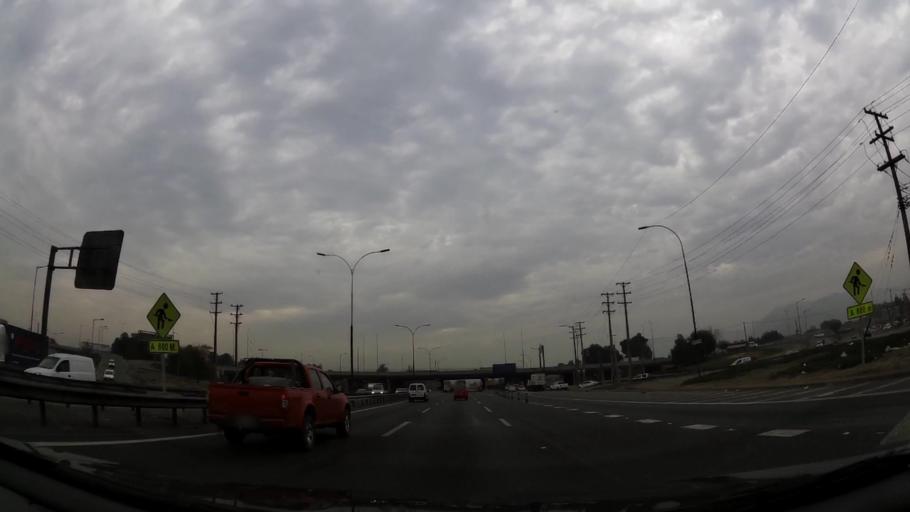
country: CL
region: Santiago Metropolitan
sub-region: Provincia de Santiago
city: Lo Prado
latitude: -33.3675
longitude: -70.6996
